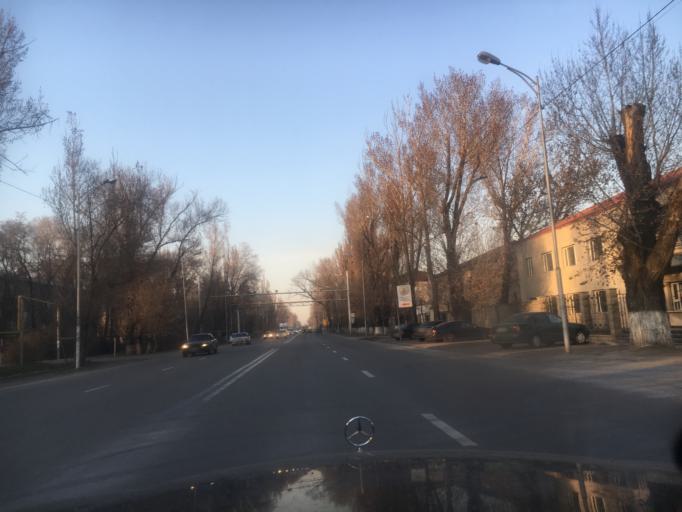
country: KZ
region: Almaty Oblysy
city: Pervomayskiy
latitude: 43.3678
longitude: 76.9872
